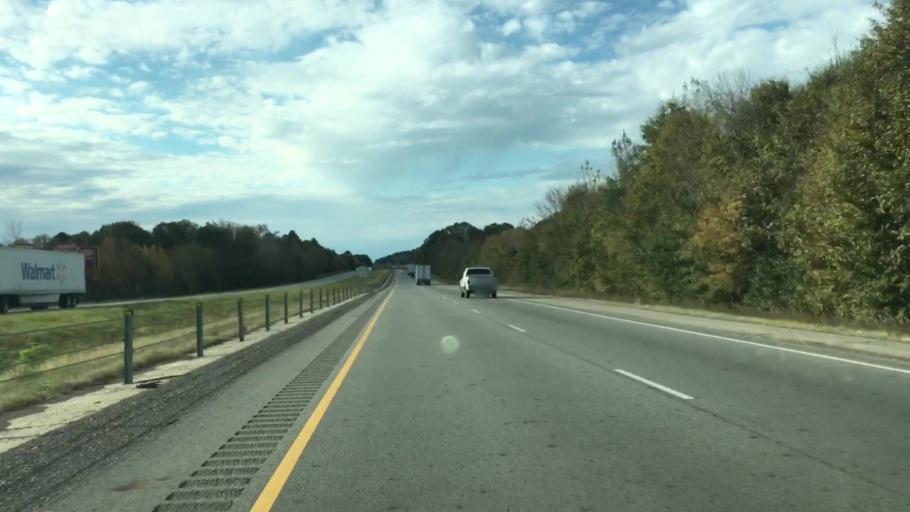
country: US
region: Arkansas
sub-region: Pope County
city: Pottsville
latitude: 35.2526
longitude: -93.0423
